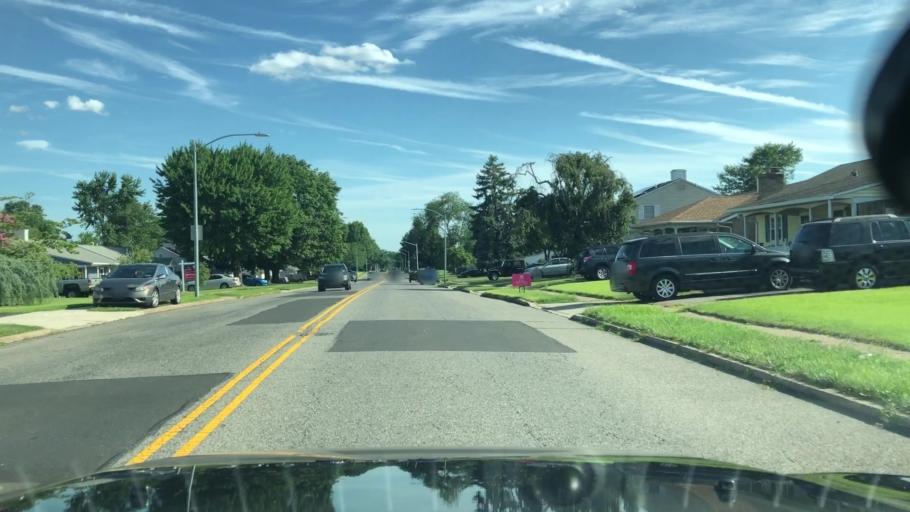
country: US
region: Pennsylvania
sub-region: Bucks County
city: Fairless Hills
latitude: 40.1880
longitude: -74.8391
